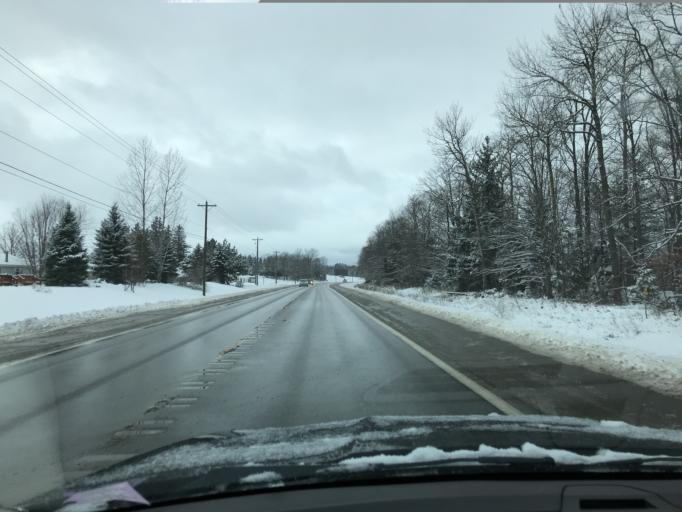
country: US
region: Michigan
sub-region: Charlevoix County
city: Charlevoix
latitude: 45.2808
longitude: -85.2345
